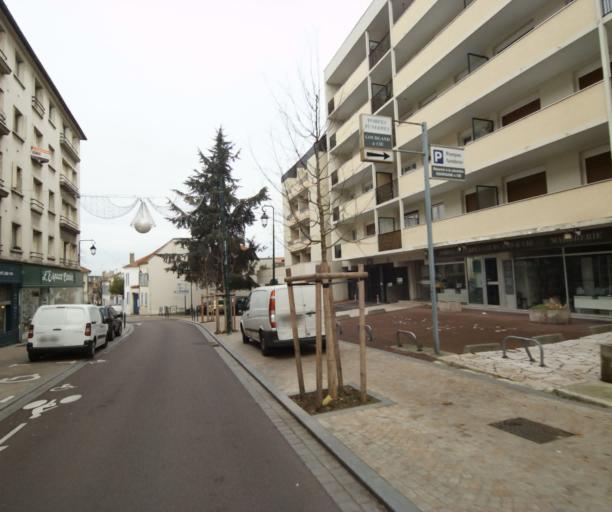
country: FR
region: Ile-de-France
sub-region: Departement des Hauts-de-Seine
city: Rueil-Malmaison
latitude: 48.8771
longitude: 2.1849
